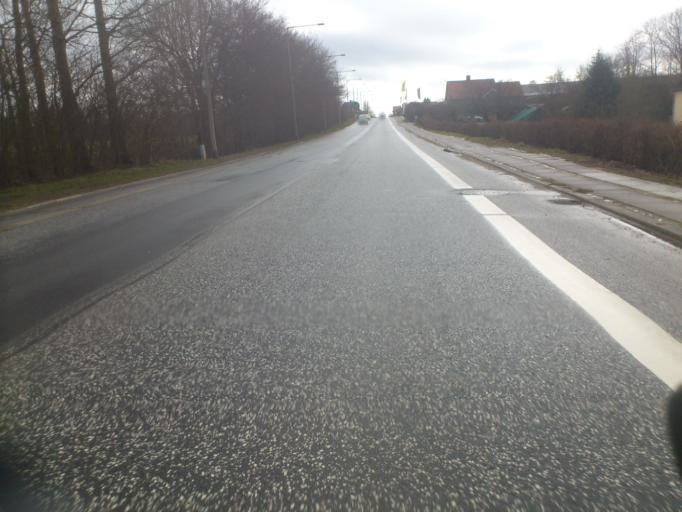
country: DK
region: South Denmark
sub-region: Fredericia Kommune
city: Fredericia
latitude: 55.5831
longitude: 9.7539
